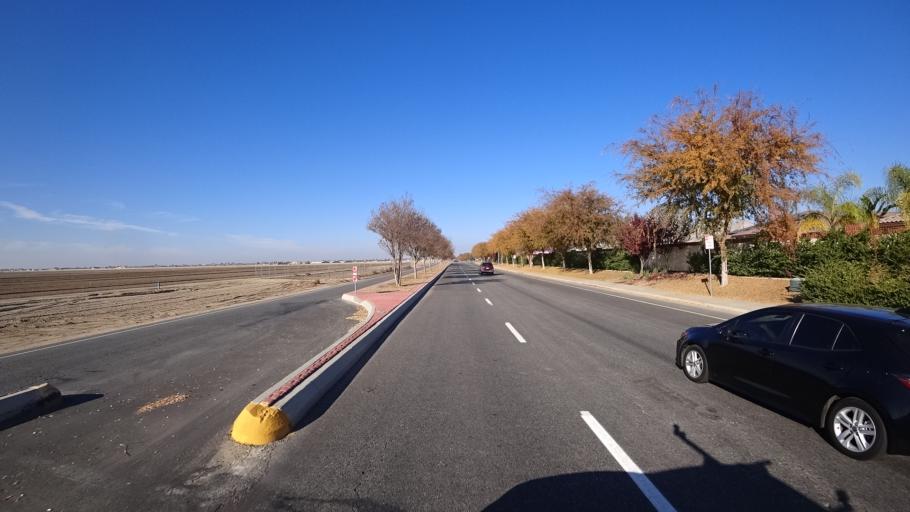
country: US
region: California
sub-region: Kern County
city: Rosedale
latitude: 35.3295
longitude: -119.1456
